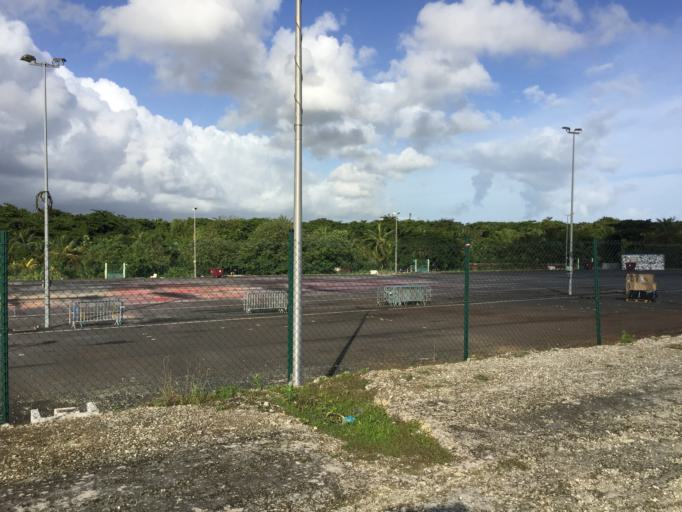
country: GP
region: Guadeloupe
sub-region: Guadeloupe
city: Baie-Mahault
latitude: 16.2424
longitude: -61.5745
